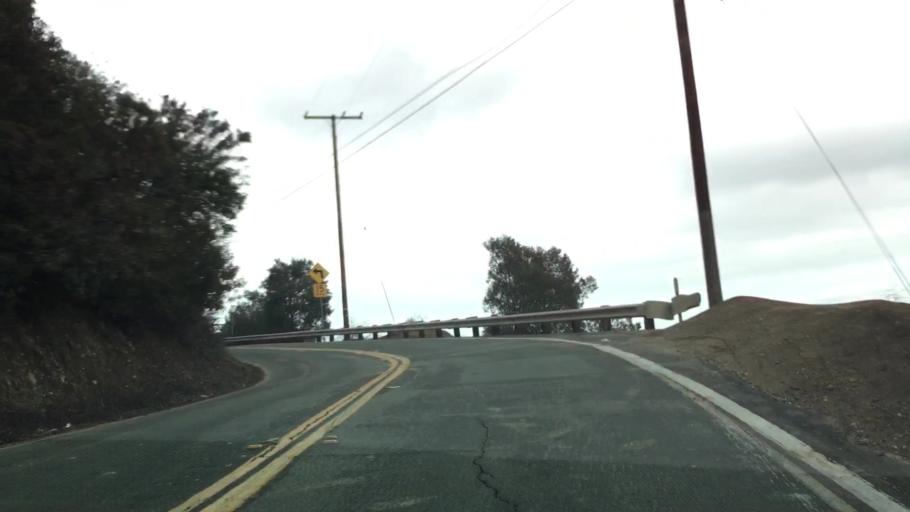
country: US
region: California
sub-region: Los Angeles County
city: Hacienda Heights
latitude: 33.9929
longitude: -117.9945
